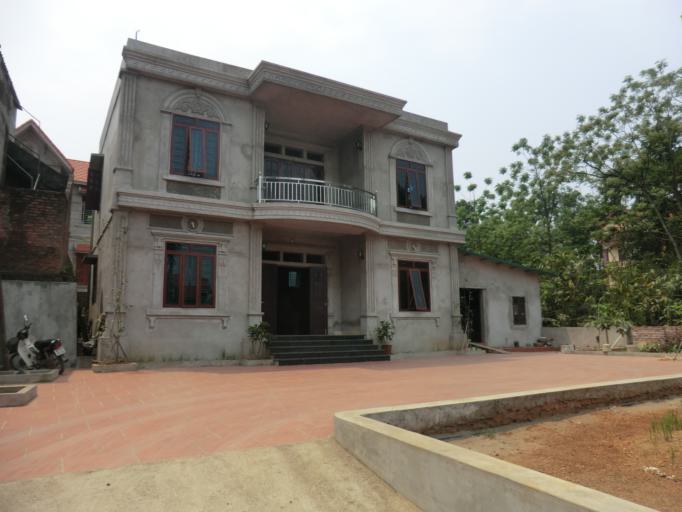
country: VN
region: Ha Noi
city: Chuc Son
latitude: 20.9452
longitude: 105.6808
